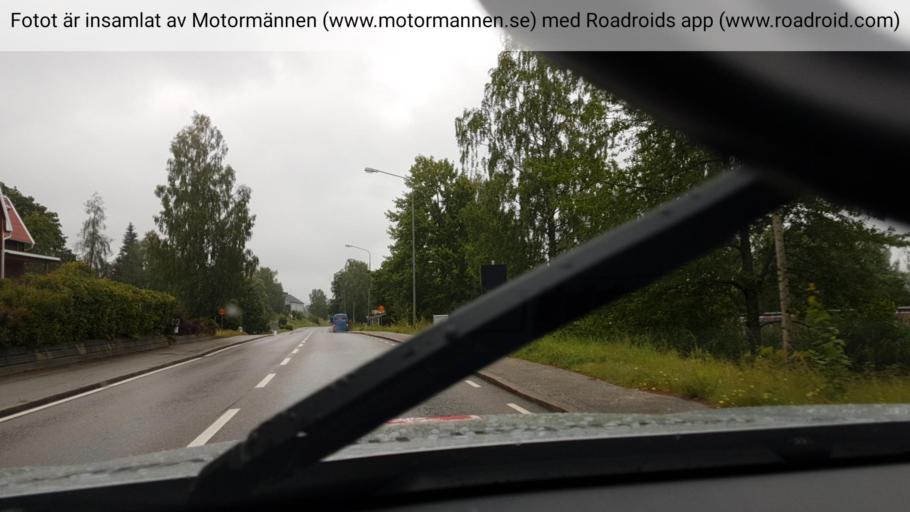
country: SE
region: Vaestra Goetaland
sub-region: Bengtsfors Kommun
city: Billingsfors
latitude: 58.9794
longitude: 12.2476
